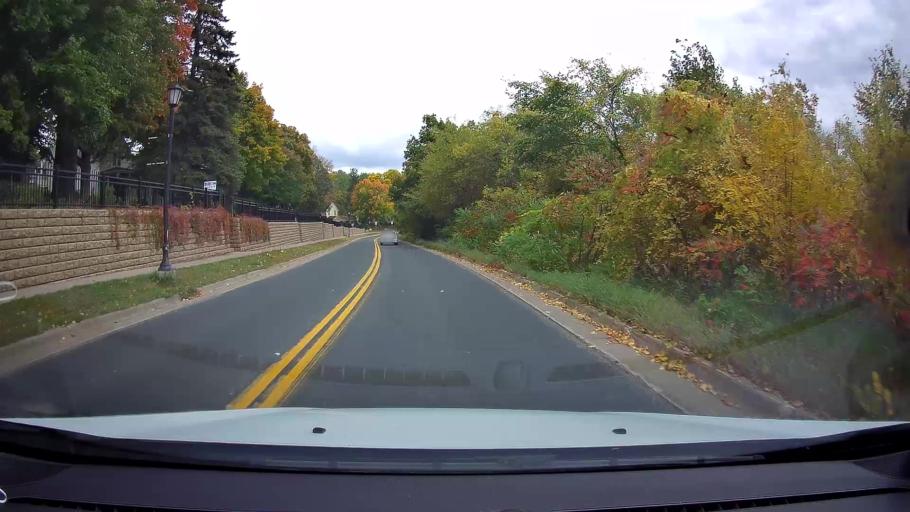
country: US
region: Minnesota
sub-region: Chisago County
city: Center City
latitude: 45.3954
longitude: -92.8181
